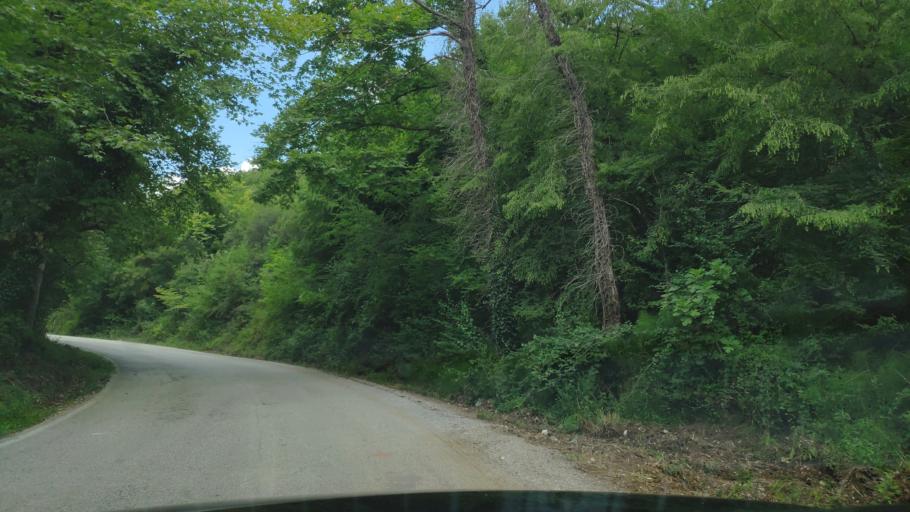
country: GR
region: Epirus
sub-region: Nomos Artas
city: Agios Dimitrios
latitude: 39.4586
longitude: 21.0369
